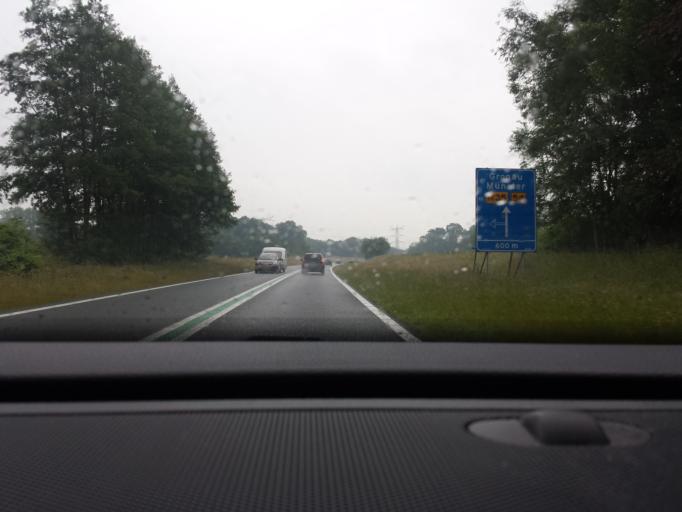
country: NL
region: Overijssel
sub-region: Gemeente Enschede
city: Enschede
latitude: 52.2031
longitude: 6.9167
